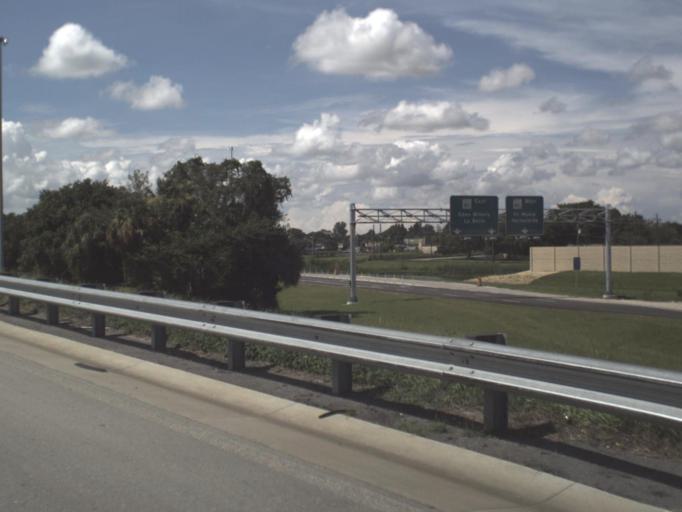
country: US
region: Florida
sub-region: Lee County
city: Tice
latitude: 26.6861
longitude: -81.7989
